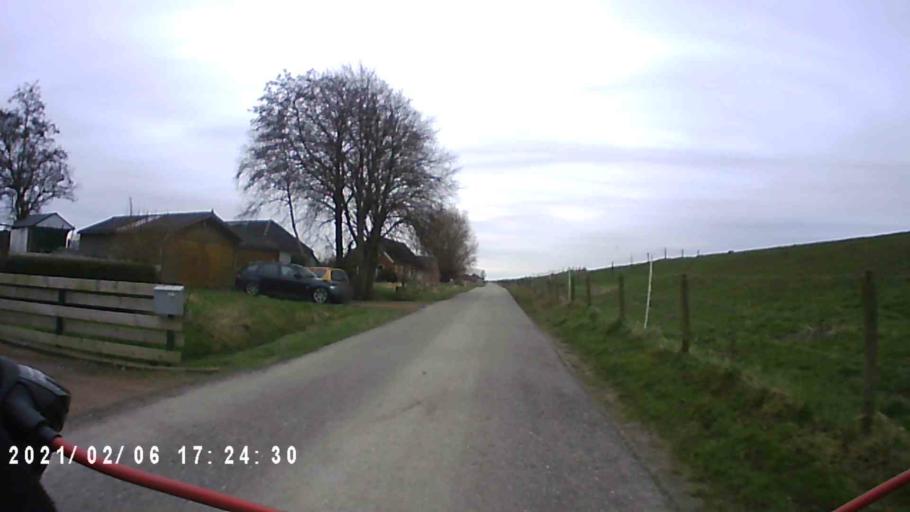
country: NL
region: Groningen
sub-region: Gemeente Appingedam
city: Appingedam
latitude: 53.4354
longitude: 6.8013
